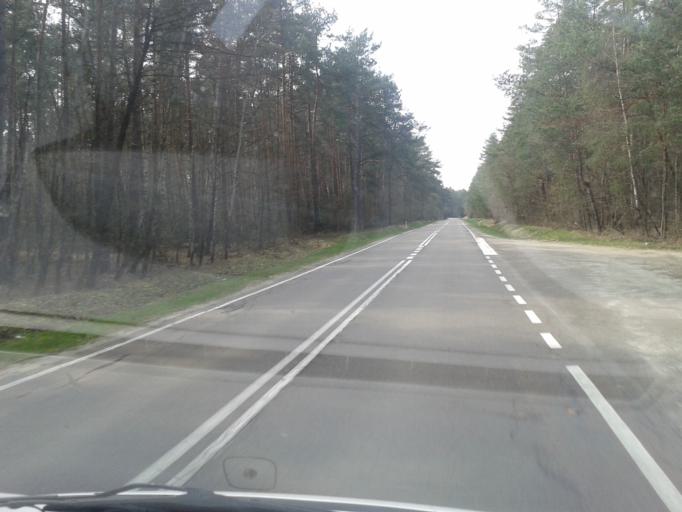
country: PL
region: Subcarpathian Voivodeship
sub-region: Powiat lubaczowski
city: Narol
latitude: 50.3692
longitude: 23.3611
